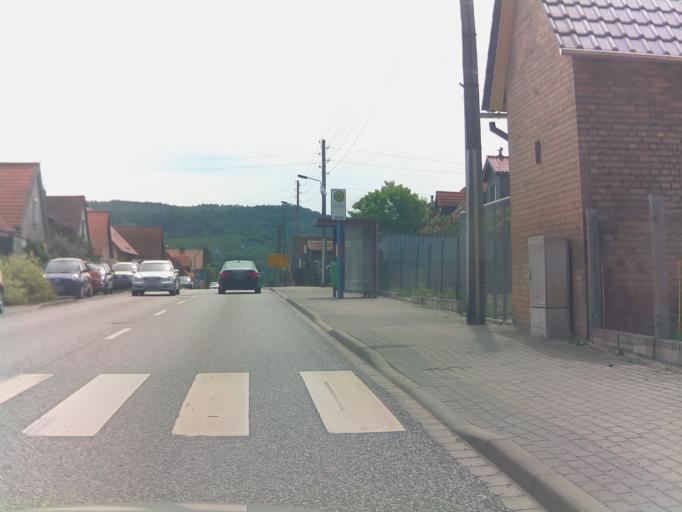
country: DE
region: Saxony-Anhalt
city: Blankenburg
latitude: 51.7759
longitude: 10.9667
